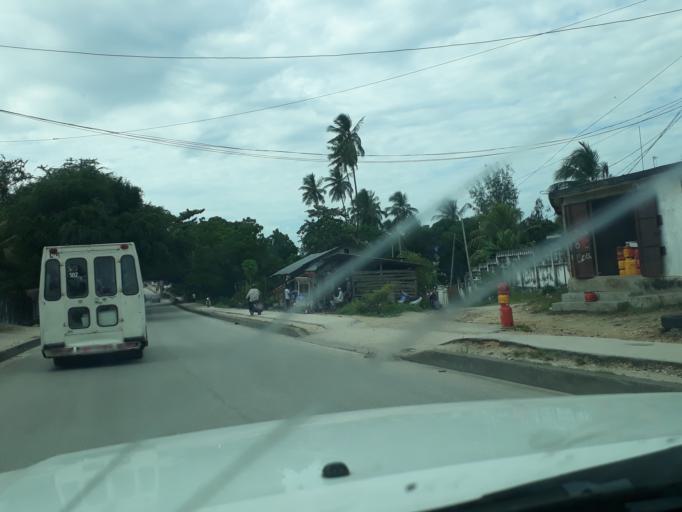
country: TZ
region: Zanzibar Urban/West
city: Zanzibar
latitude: -6.1011
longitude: 39.2181
